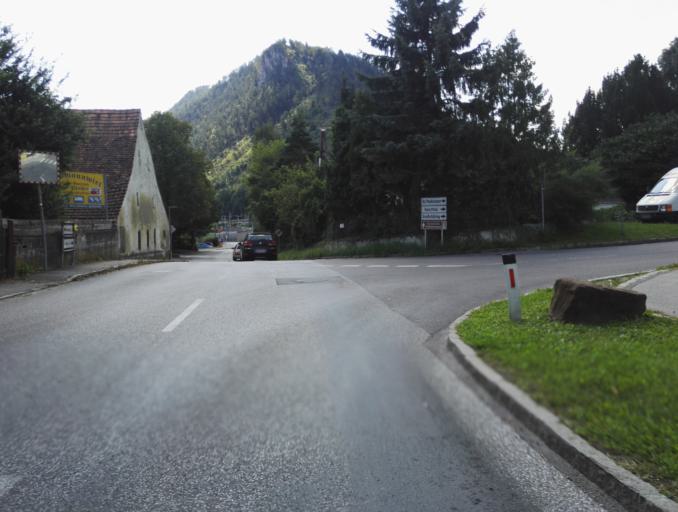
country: AT
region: Styria
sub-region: Politischer Bezirk Graz-Umgebung
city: Deutschfeistritz
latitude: 47.1780
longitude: 15.3217
